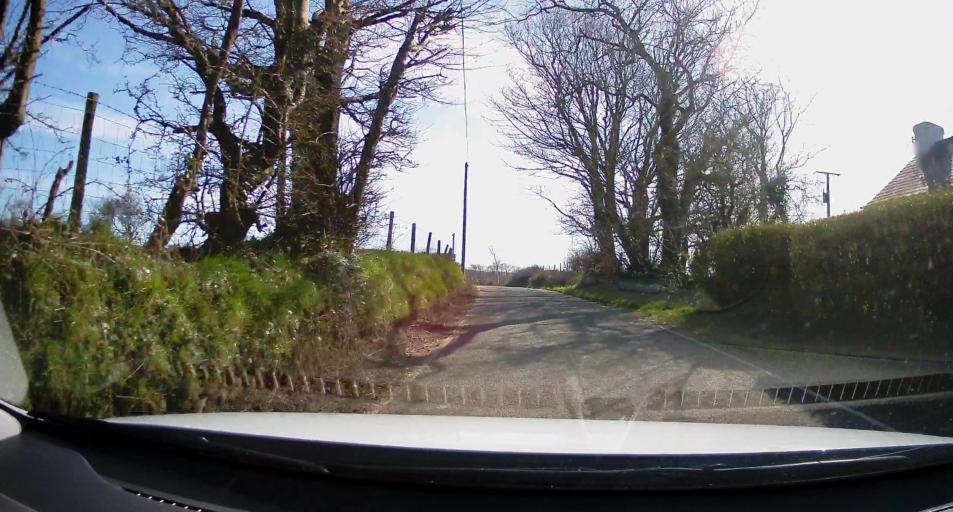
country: GB
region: Wales
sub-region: County of Ceredigion
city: Lledrod
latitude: 52.2964
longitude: -4.0691
